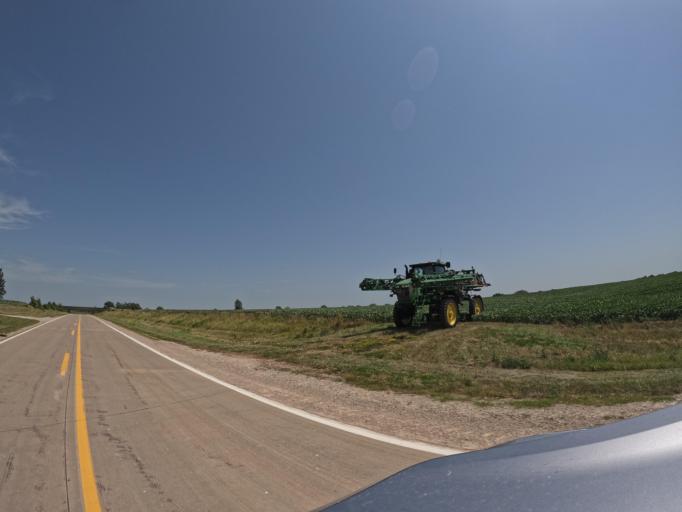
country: US
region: Iowa
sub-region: Henry County
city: Mount Pleasant
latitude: 40.9816
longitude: -91.6236
